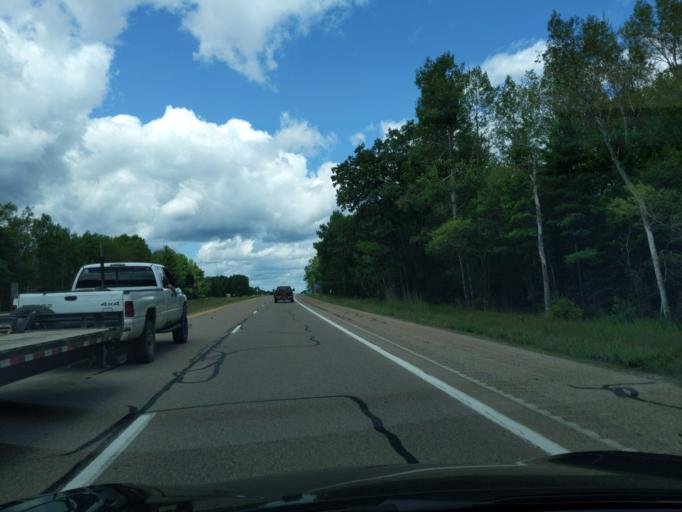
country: US
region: Michigan
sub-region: Roscommon County
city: Houghton Lake
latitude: 44.3249
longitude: -84.8070
